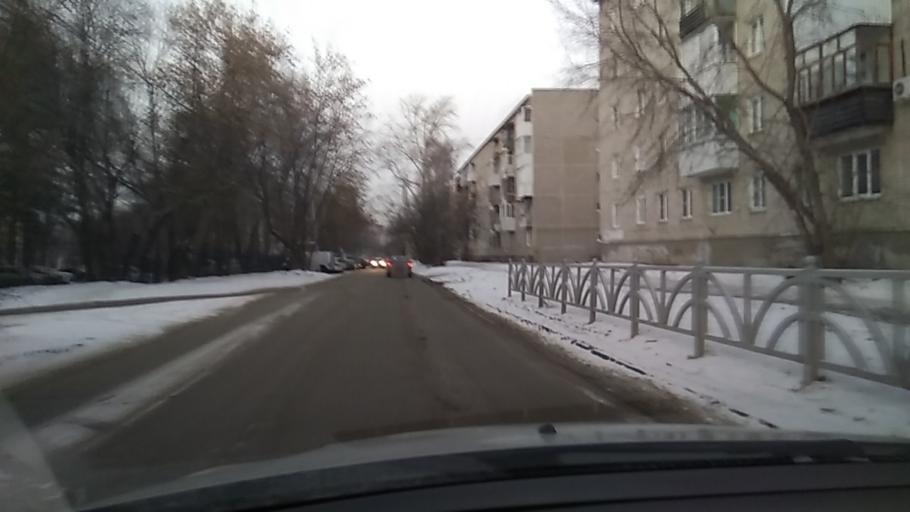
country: RU
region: Sverdlovsk
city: Istok
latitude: 56.7628
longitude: 60.7114
